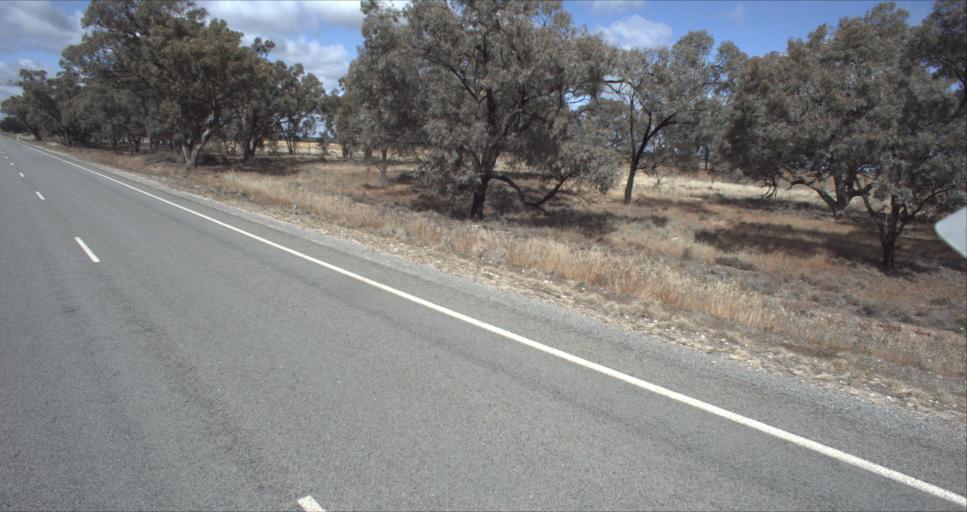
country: AU
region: New South Wales
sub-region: Murrumbidgee Shire
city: Darlington Point
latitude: -34.5657
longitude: 146.1682
